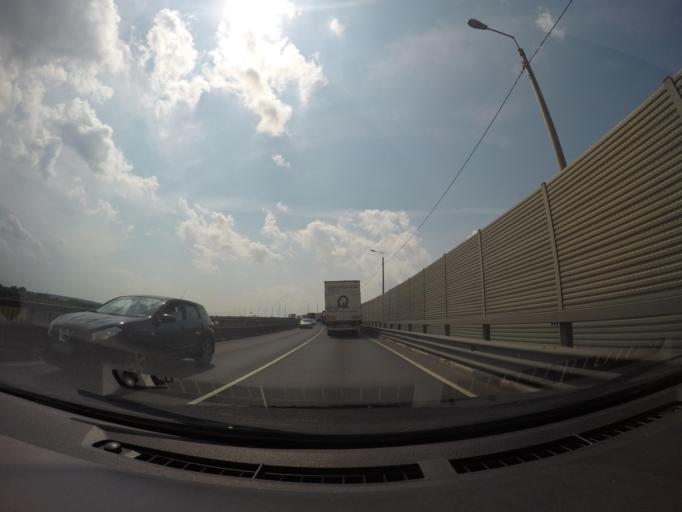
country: RU
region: Moskovskaya
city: Bronnitsy
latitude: 55.4279
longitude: 38.2969
